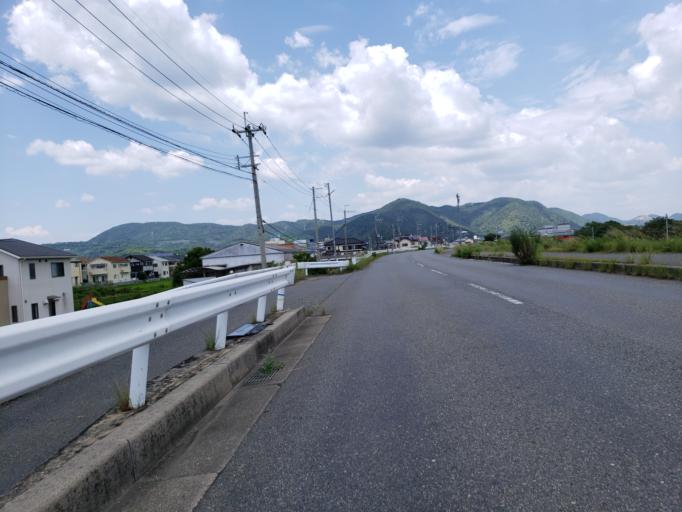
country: JP
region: Hyogo
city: Kariya
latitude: 34.7442
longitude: 134.3920
